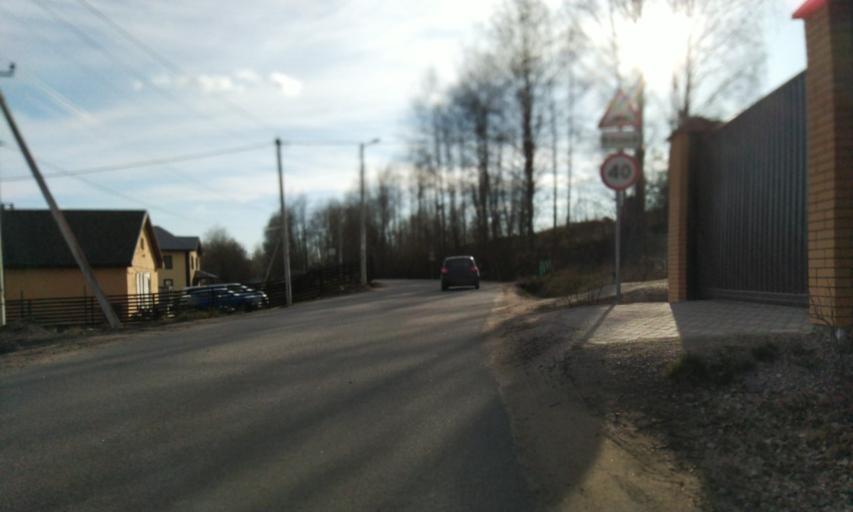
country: RU
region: Leningrad
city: Bugry
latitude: 60.1127
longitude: 30.4257
